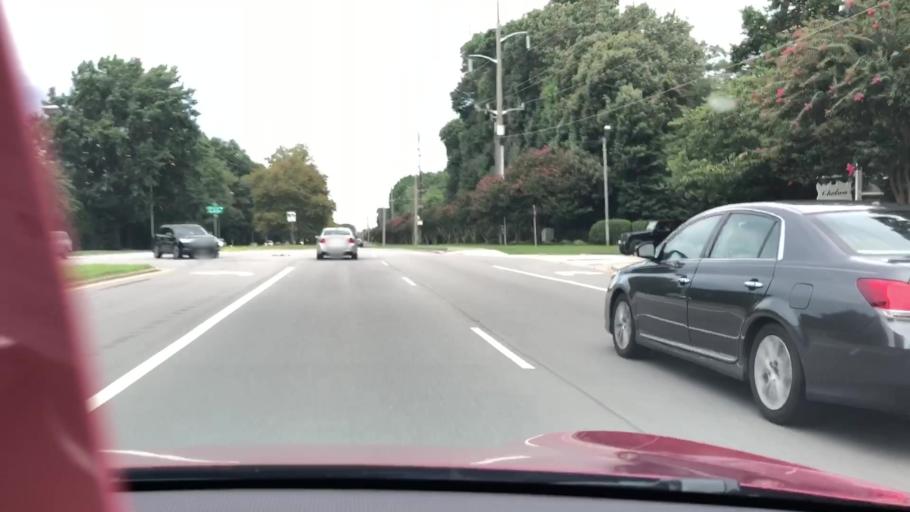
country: US
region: Virginia
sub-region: City of Virginia Beach
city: Virginia Beach
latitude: 36.8916
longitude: -76.0548
